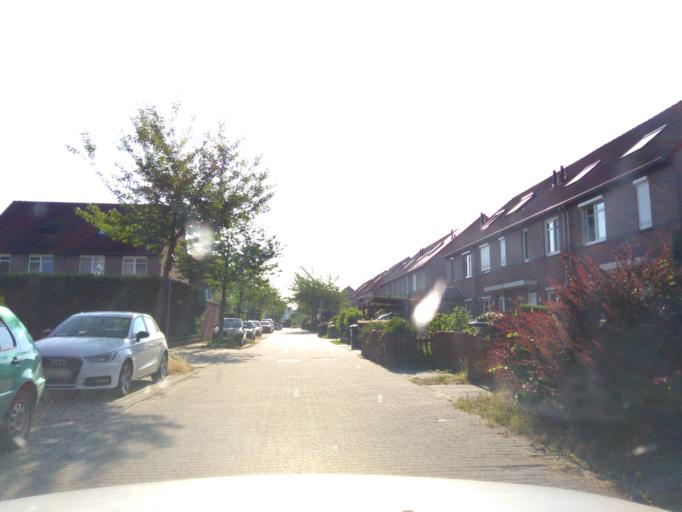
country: DE
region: Brandenburg
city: Dallgow-Doeberitz
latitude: 52.5608
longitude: 13.0595
